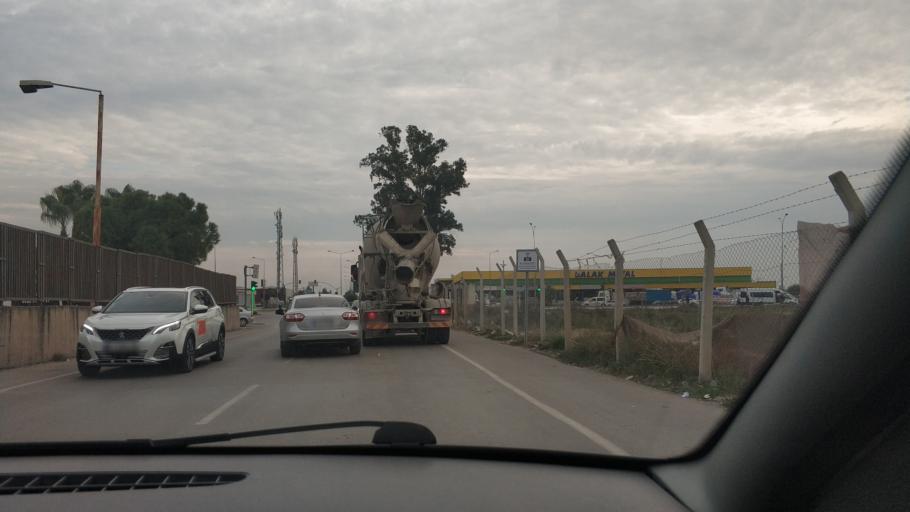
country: TR
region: Adana
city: Seyhan
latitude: 36.9974
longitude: 35.2600
